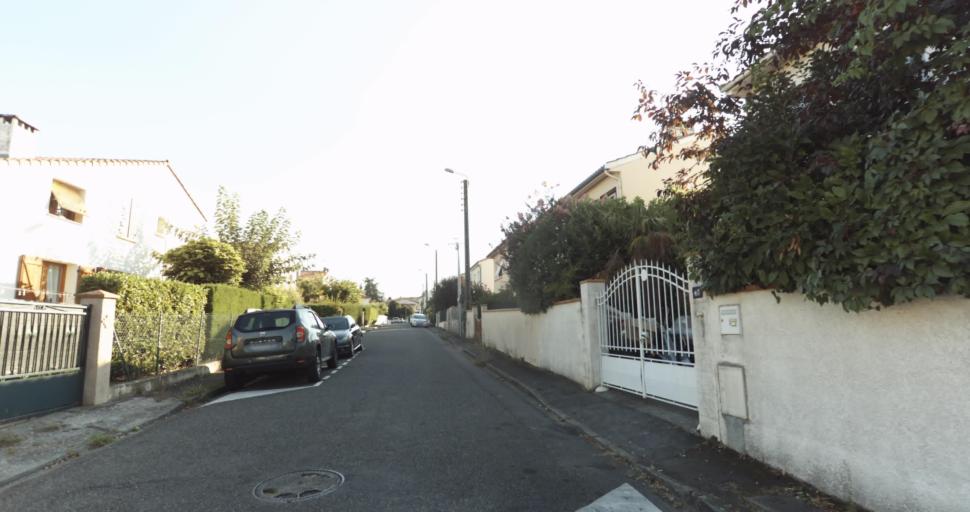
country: FR
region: Midi-Pyrenees
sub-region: Departement de la Haute-Garonne
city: L'Union
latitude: 43.6571
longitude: 1.4763
